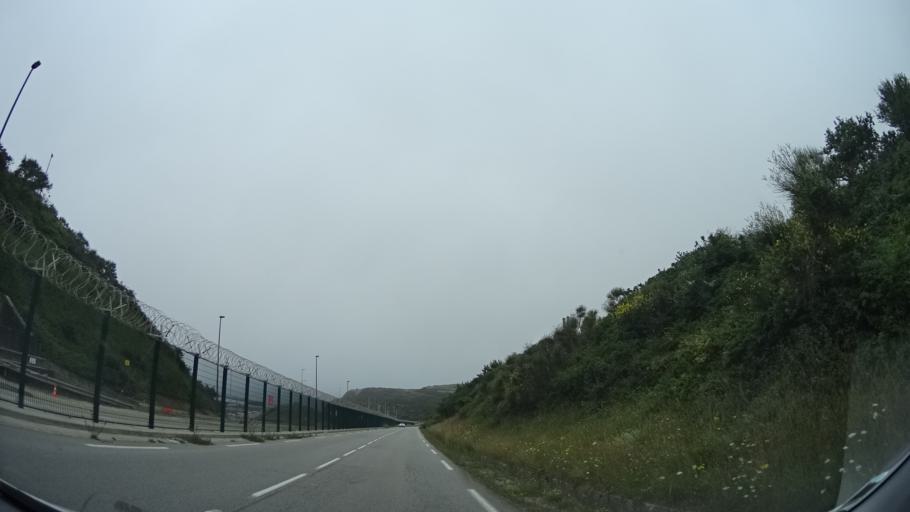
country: FR
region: Lower Normandy
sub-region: Departement de la Manche
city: Flamanville
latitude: 49.5399
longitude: -1.8745
